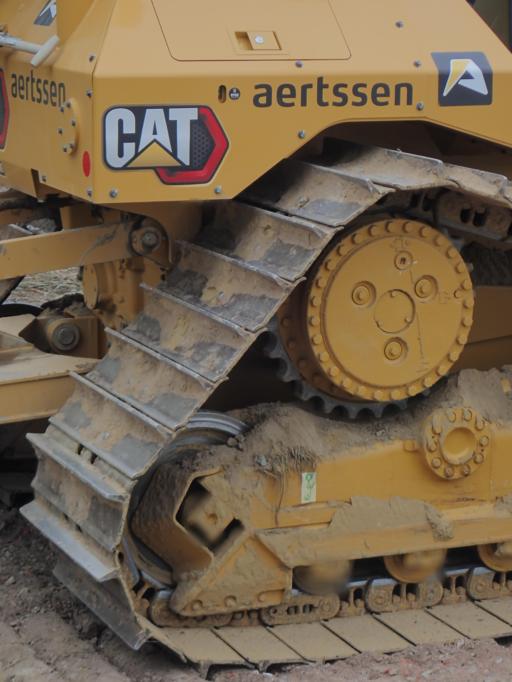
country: BE
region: Flanders
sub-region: Provincie Oost-Vlaanderen
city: Lebbeke
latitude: 51.0476
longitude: 4.1451
